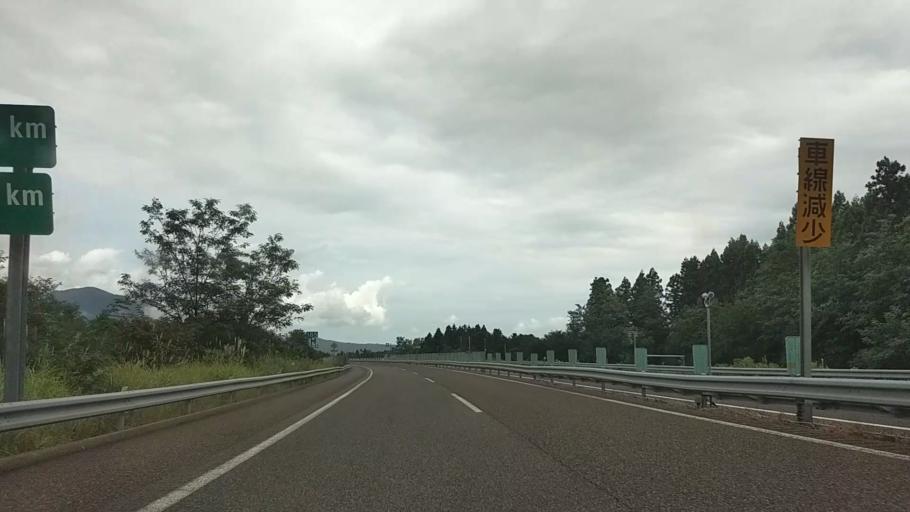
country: JP
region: Niigata
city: Arai
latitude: 36.9735
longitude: 138.2214
